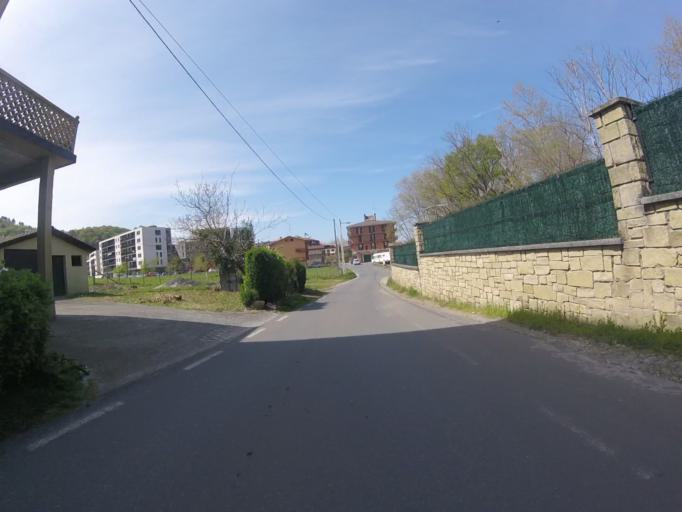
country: ES
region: Basque Country
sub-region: Provincia de Guipuzcoa
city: Lezo
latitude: 43.2928
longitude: -1.8534
